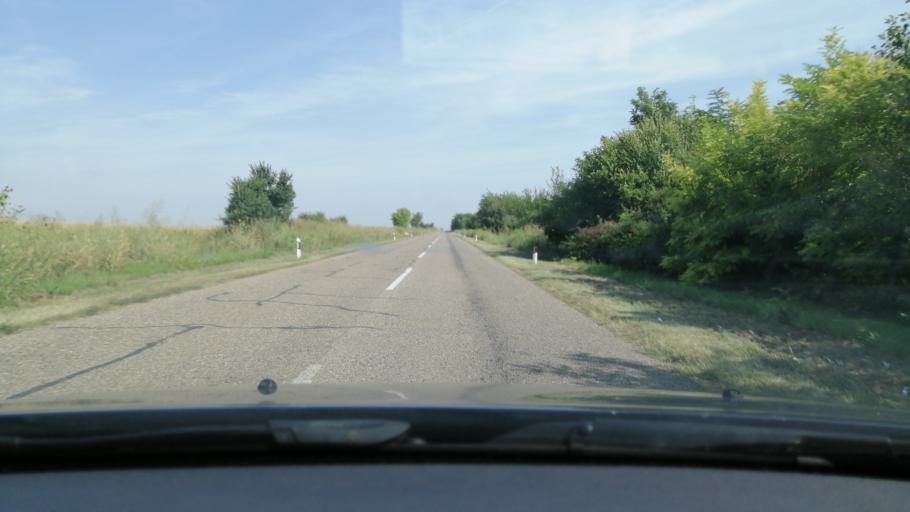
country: RS
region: Autonomna Pokrajina Vojvodina
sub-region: Juznobanatski Okrug
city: Kovacica
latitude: 45.1488
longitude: 20.6167
